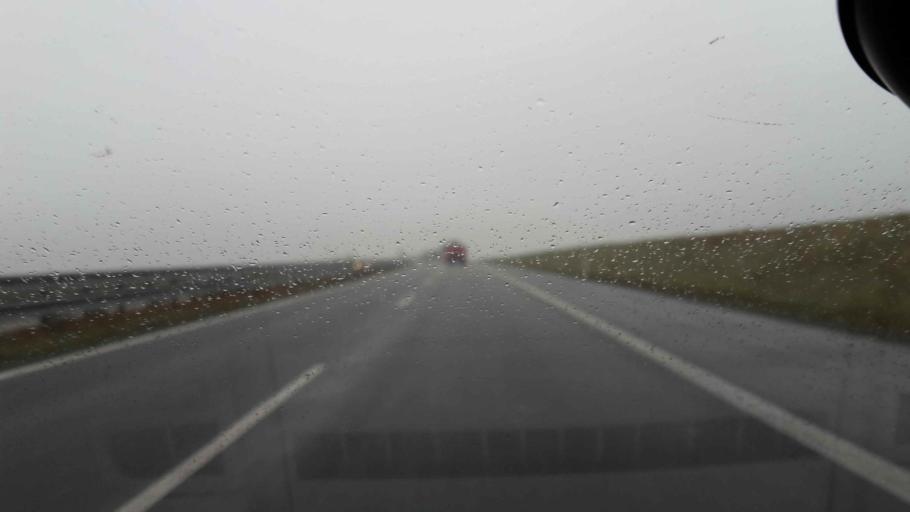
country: CZ
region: South Moravian
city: Blazovice
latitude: 49.1802
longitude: 16.7874
